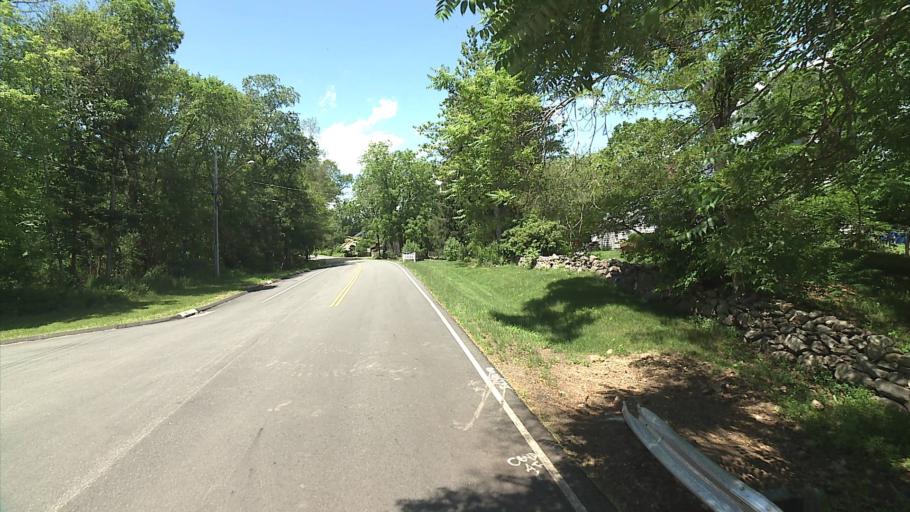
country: US
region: Connecticut
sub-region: New London County
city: Old Mystic
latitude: 41.3838
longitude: -71.9400
